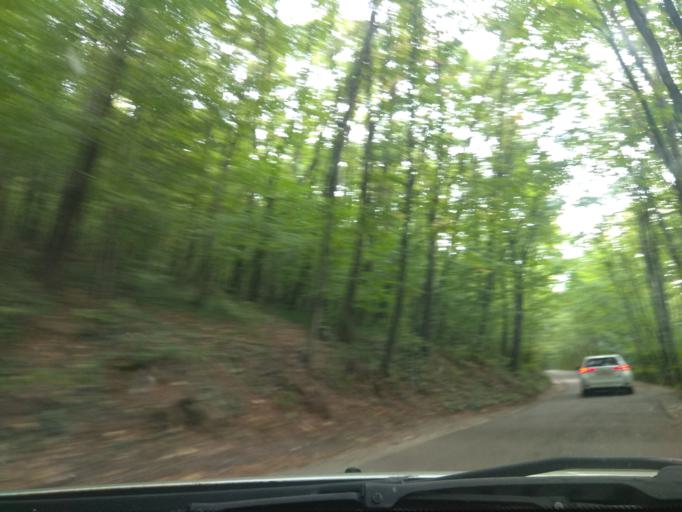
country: HU
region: Borsod-Abauj-Zemplen
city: Saly
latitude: 48.0651
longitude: 20.6691
